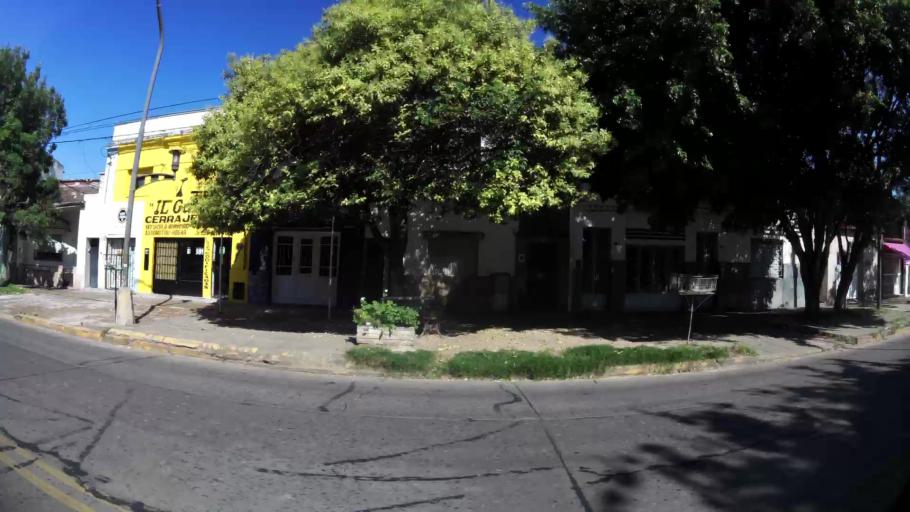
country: AR
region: Santa Fe
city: Santa Fe de la Vera Cruz
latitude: -31.6253
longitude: -60.6895
